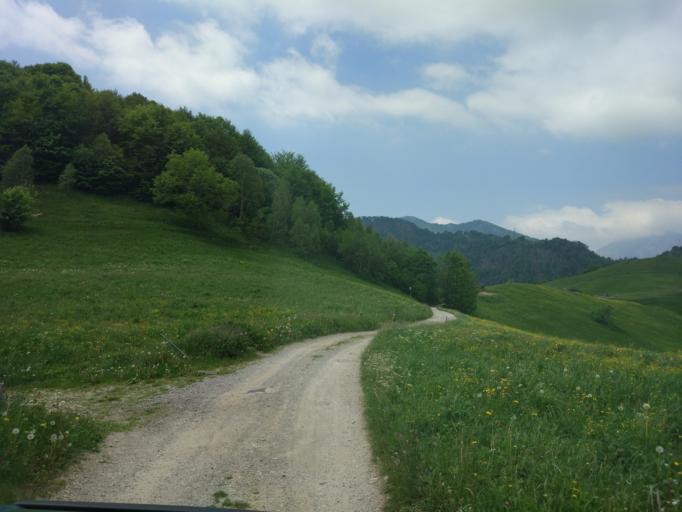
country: IT
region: Lombardy
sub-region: Provincia di Lecco
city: Morterone
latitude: 45.9025
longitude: 9.4915
